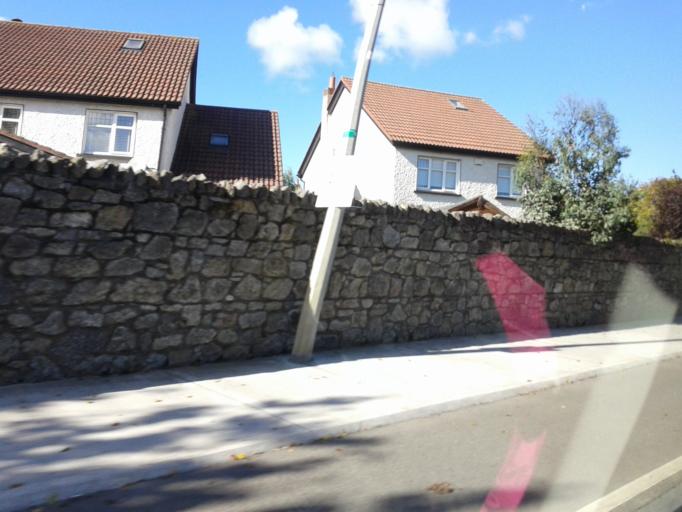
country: IE
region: Leinster
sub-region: An Mhi
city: Ashbourne
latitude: 53.5060
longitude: -6.3928
